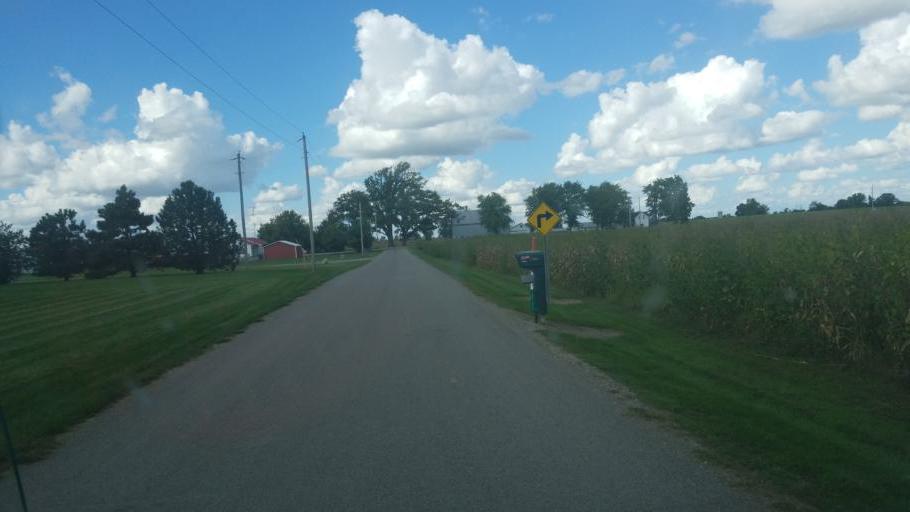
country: US
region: Ohio
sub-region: Hardin County
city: Kenton
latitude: 40.5465
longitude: -83.5446
